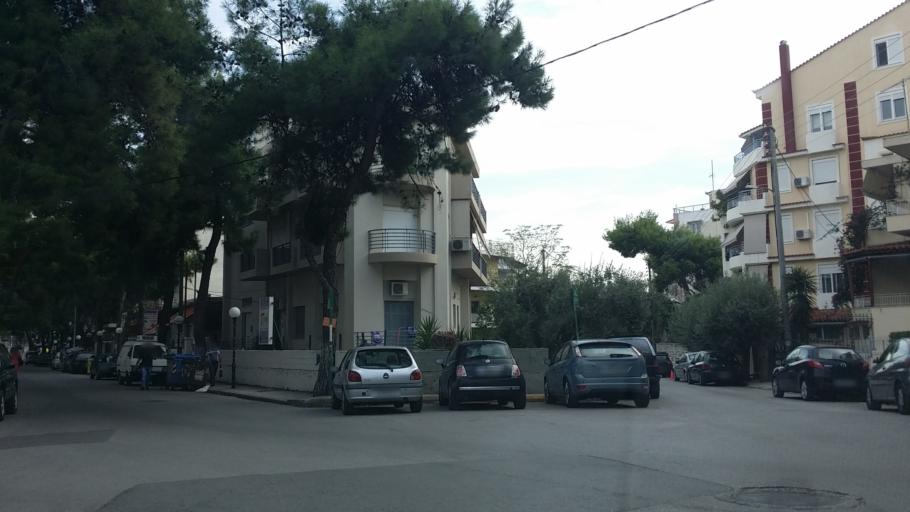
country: GR
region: Attica
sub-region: Nomarchia Athinas
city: Irakleio
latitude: 38.0511
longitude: 23.7624
